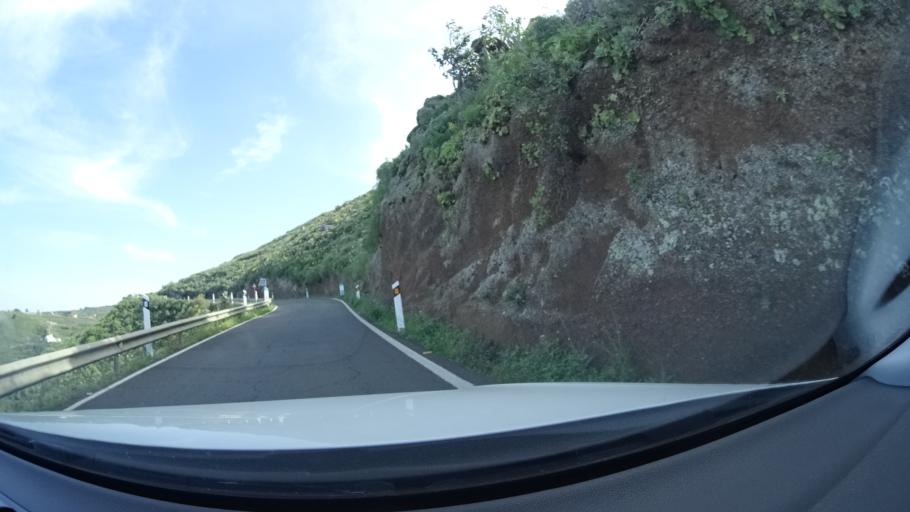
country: ES
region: Canary Islands
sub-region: Provincia de Las Palmas
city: Guia
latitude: 28.1108
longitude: -15.6386
